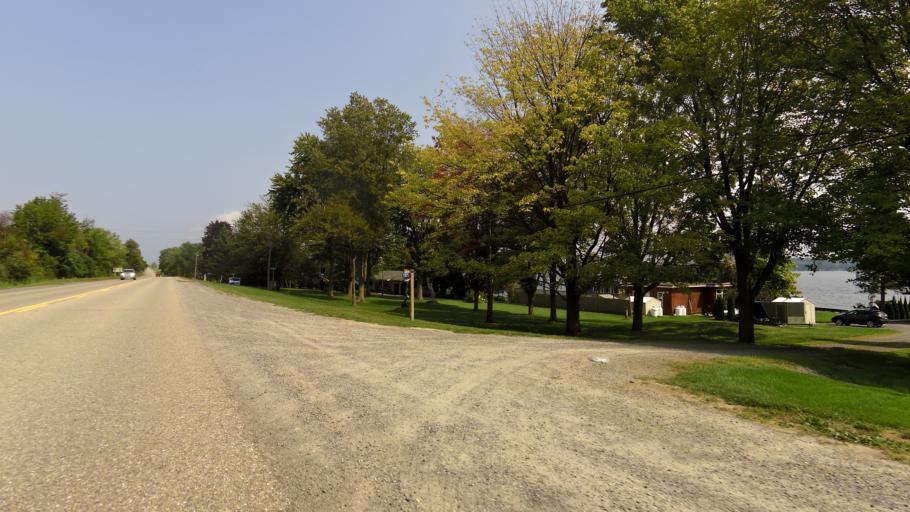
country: CA
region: Ontario
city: Prescott
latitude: 44.6532
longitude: -75.5897
